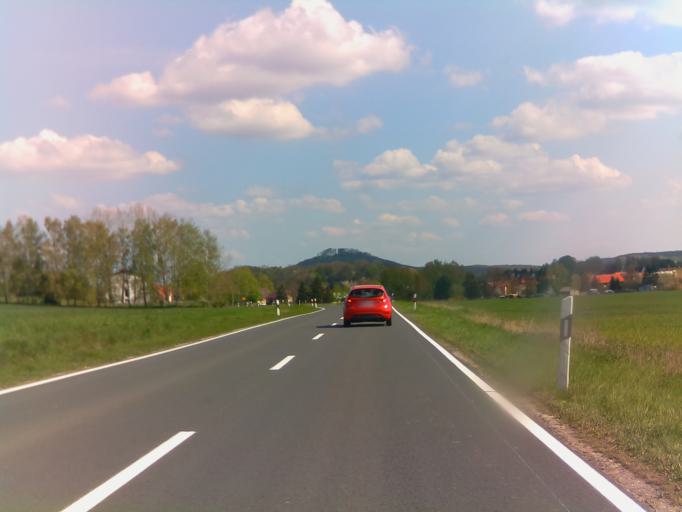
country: DE
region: Thuringia
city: Westhausen
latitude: 50.3609
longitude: 10.6770
